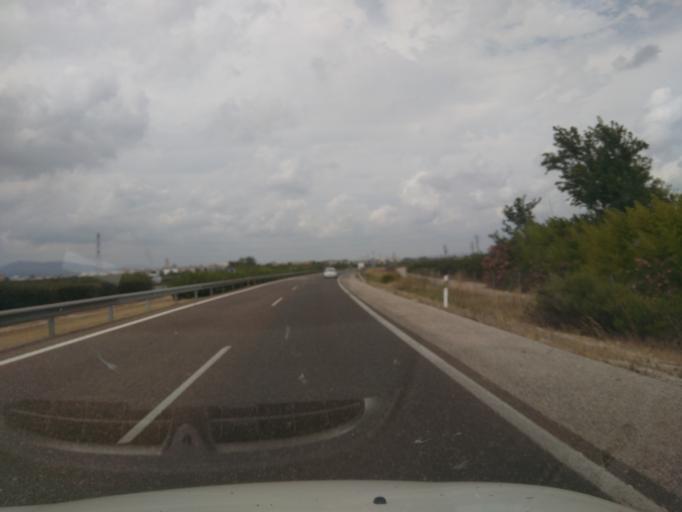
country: ES
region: Valencia
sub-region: Provincia de Valencia
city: L'Alcudia
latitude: 39.1862
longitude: -0.4914
